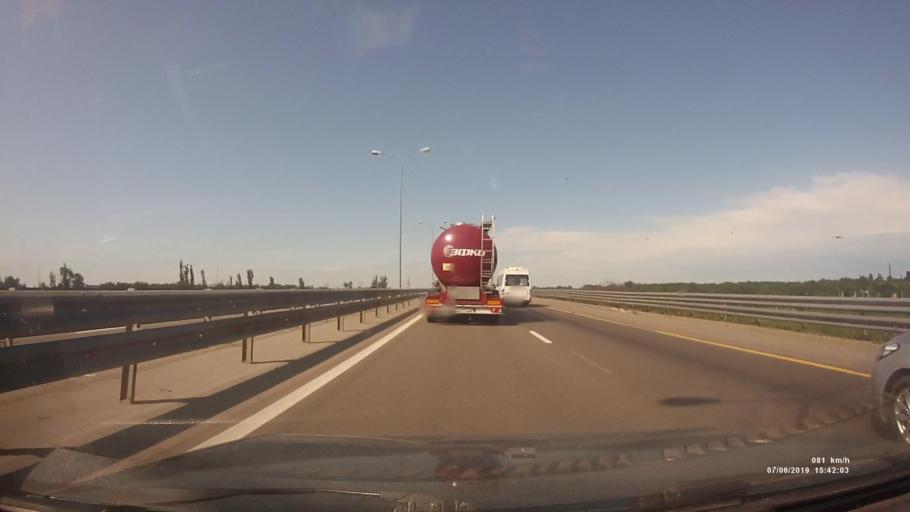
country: RU
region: Rostov
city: Mayskiy
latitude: 47.6982
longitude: 40.0886
